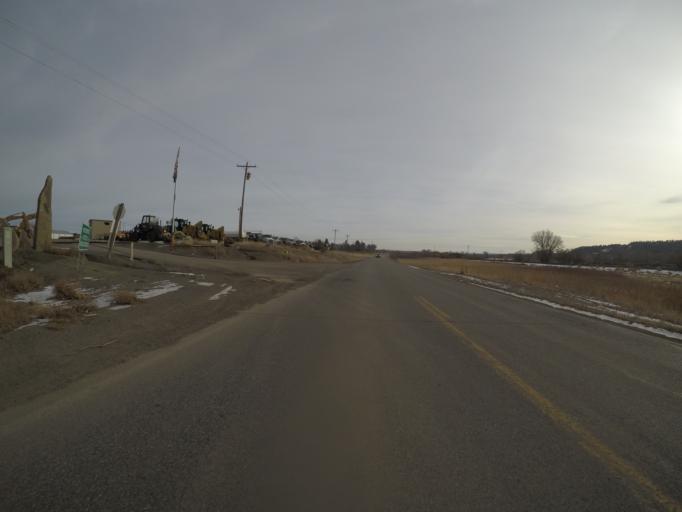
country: US
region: Montana
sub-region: Stillwater County
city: Columbus
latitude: 45.6420
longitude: -109.2806
